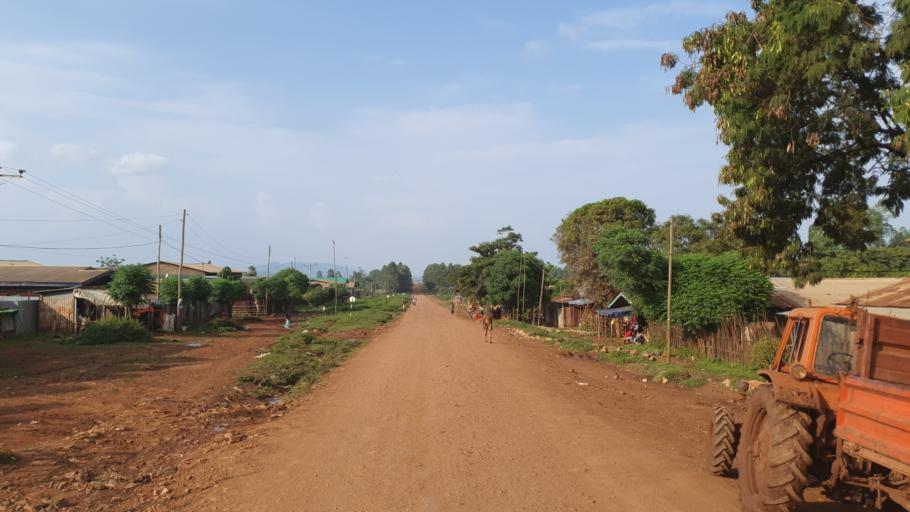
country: ET
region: Oromiya
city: Shambu
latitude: 9.3778
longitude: 36.5286
